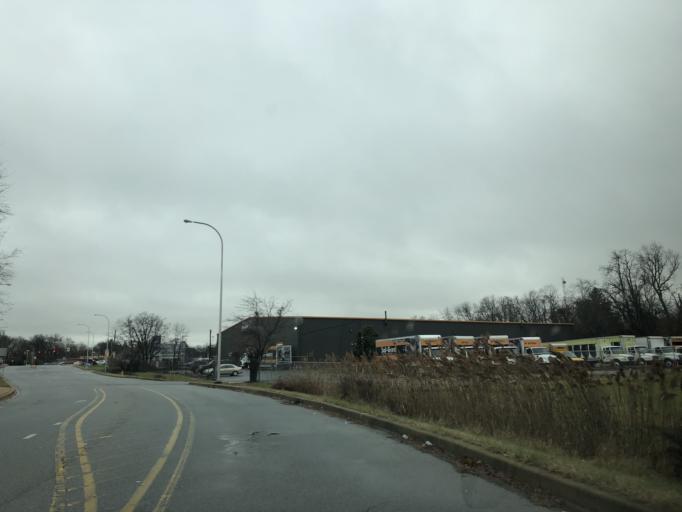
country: US
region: Delaware
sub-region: New Castle County
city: Wilmington Manor
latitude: 39.7133
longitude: -75.5645
